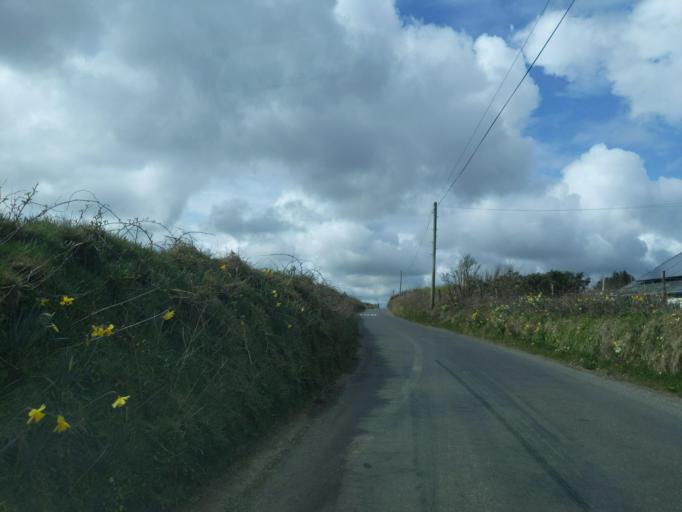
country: GB
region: England
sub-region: Cornwall
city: Camelford
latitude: 50.6270
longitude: -4.5955
